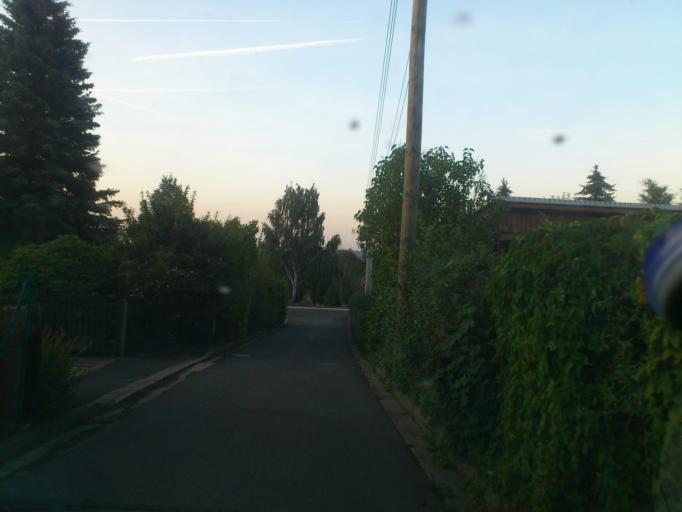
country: DE
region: Saxony
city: Jahnsdorf
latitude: 50.7523
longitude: 12.8650
